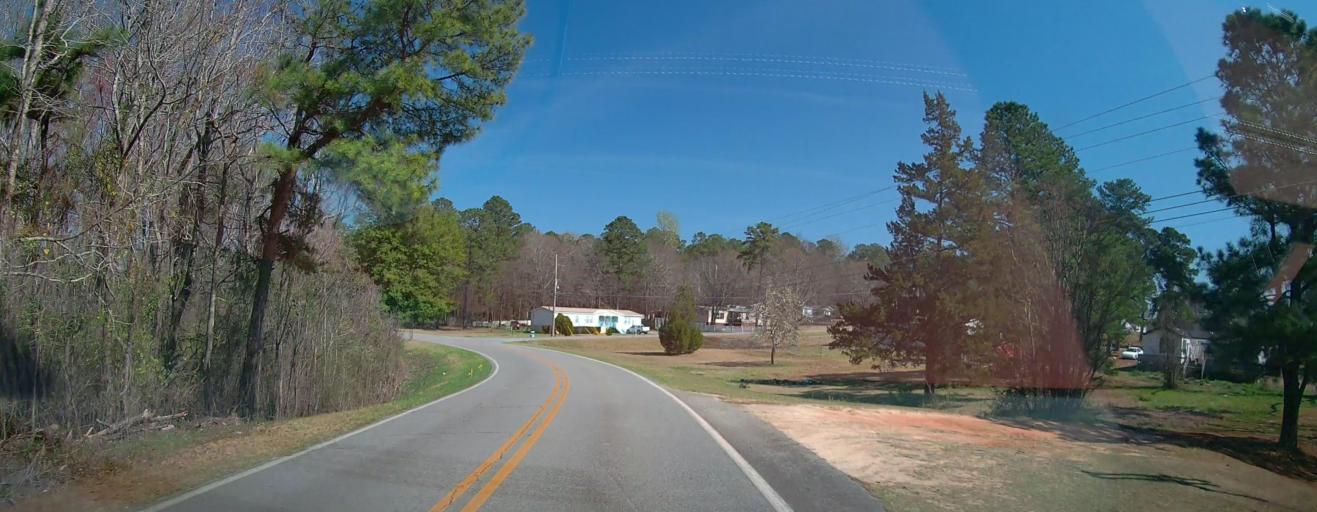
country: US
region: Georgia
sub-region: Jones County
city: Gray
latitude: 32.9139
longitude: -83.5352
